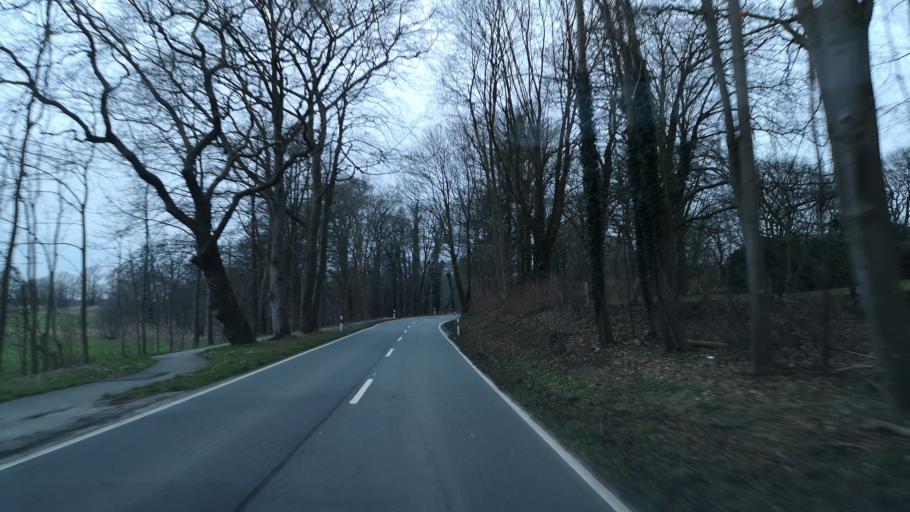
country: DE
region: Schleswig-Holstein
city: Munsterdorf
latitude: 53.9157
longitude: 9.5325
